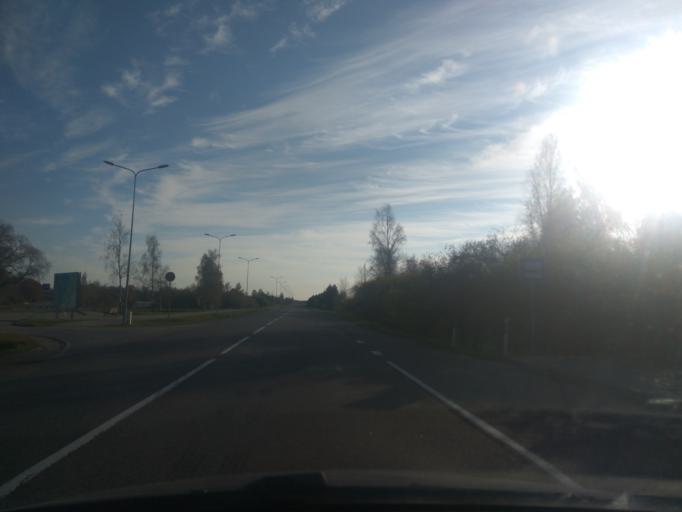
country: LV
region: Ventspils
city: Ventspils
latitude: 57.3595
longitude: 21.5633
